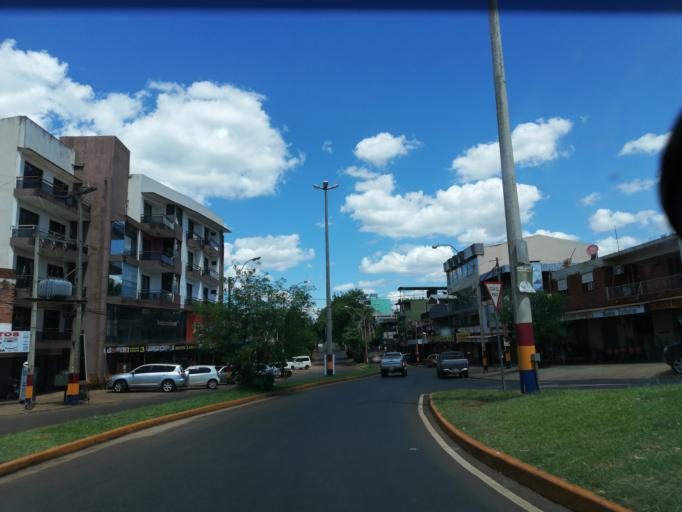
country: PY
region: Itapua
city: Encarnacion
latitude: -27.3534
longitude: -55.8583
